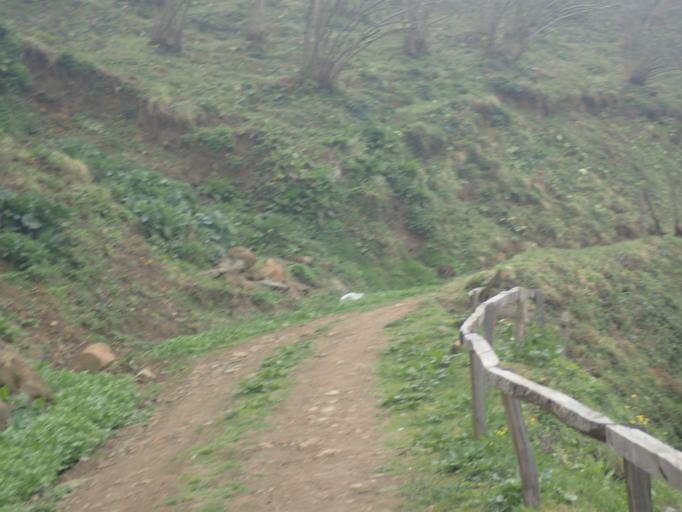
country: TR
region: Ordu
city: Camas
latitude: 40.9001
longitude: 37.5573
